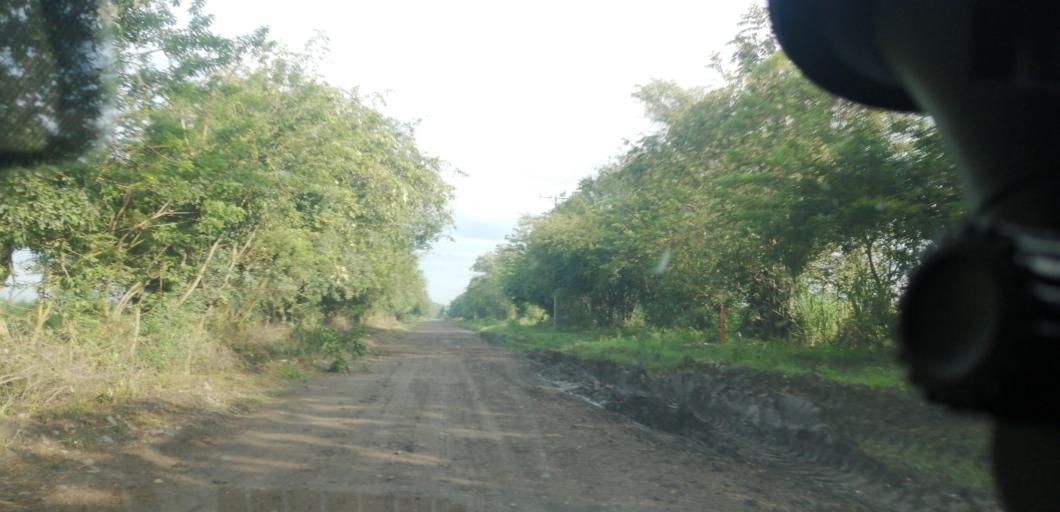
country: CO
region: Valle del Cauca
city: Palmira
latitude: 3.5465
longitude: -76.3618
